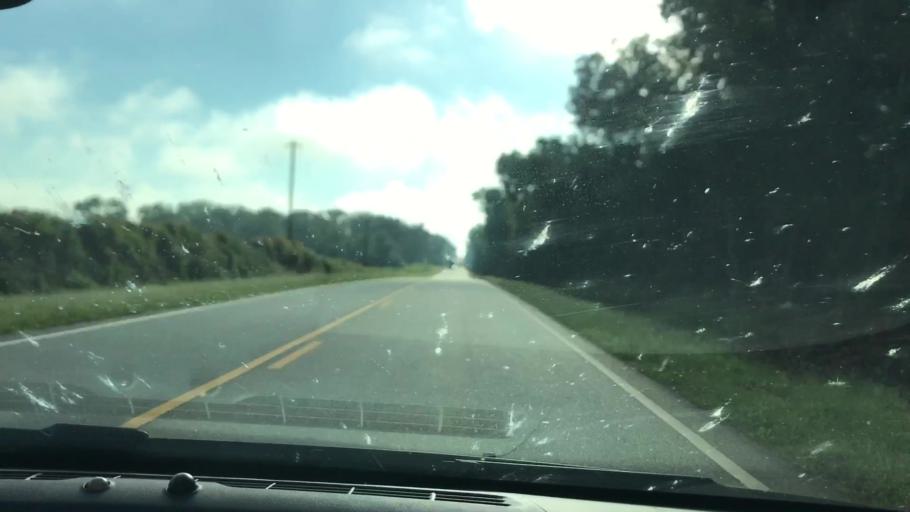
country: US
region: Georgia
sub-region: Terrell County
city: Dawson
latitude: 31.7700
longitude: -84.4962
